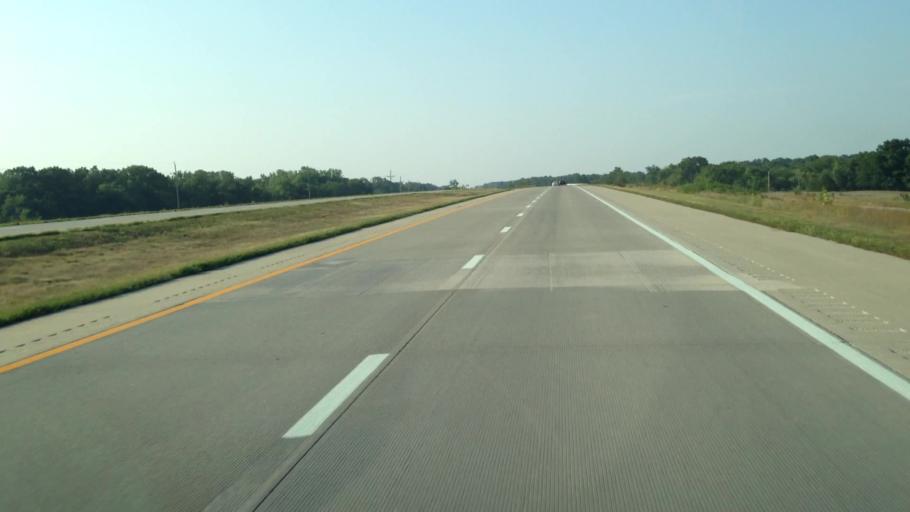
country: US
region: Kansas
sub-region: Douglas County
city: Baldwin City
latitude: 38.7351
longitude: -95.2677
